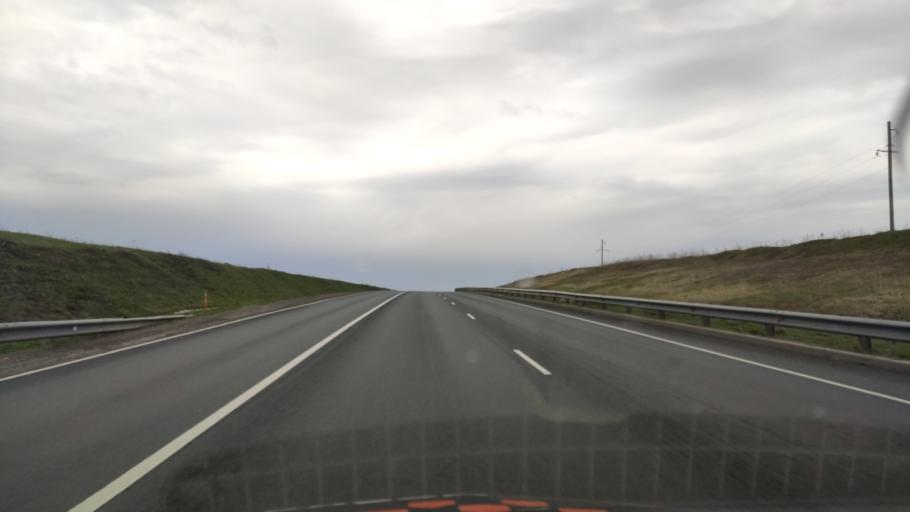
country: RU
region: Voronezj
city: Latnaya
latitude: 51.6491
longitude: 38.7369
